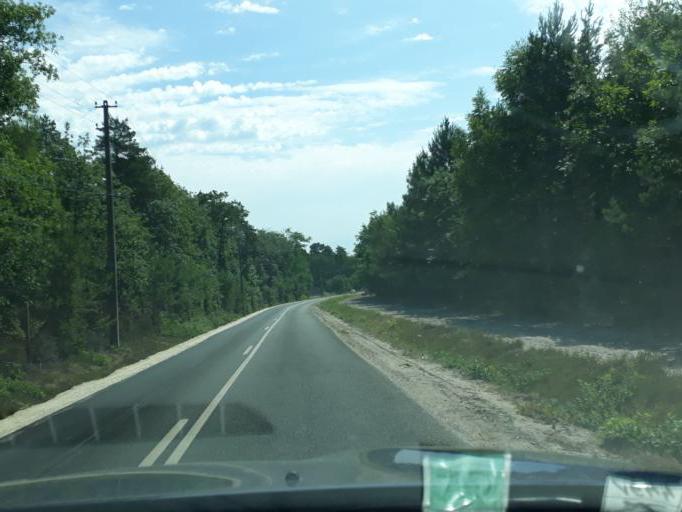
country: FR
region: Centre
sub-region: Departement du Loir-et-Cher
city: Vouzon
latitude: 47.6483
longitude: 2.0254
